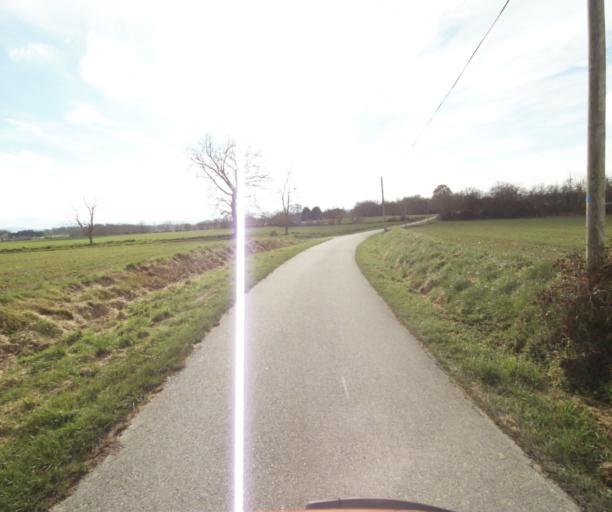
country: FR
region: Midi-Pyrenees
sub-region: Departement de l'Ariege
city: La Tour-du-Crieu
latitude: 43.1224
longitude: 1.6927
